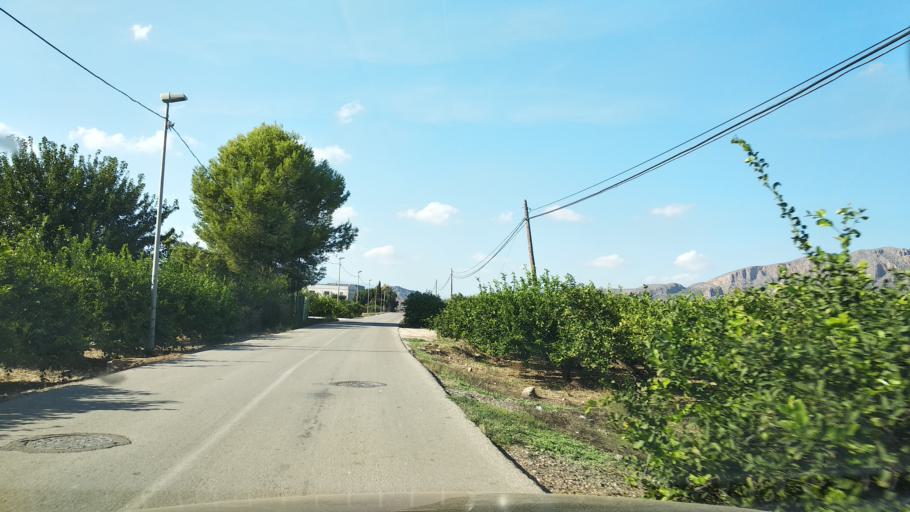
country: ES
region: Murcia
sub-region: Murcia
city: Santomera
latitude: 38.0492
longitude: -1.0395
